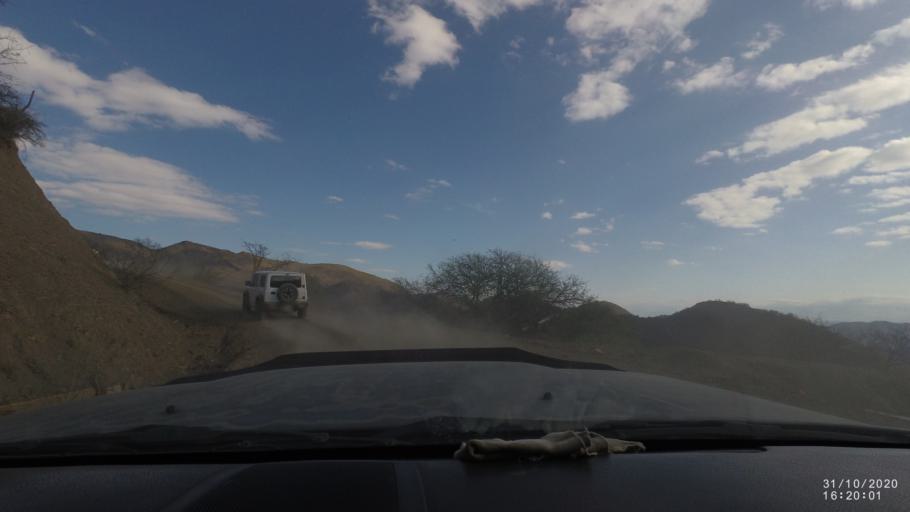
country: BO
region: Chuquisaca
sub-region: Provincia Zudanez
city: Mojocoya
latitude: -18.3978
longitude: -64.6034
